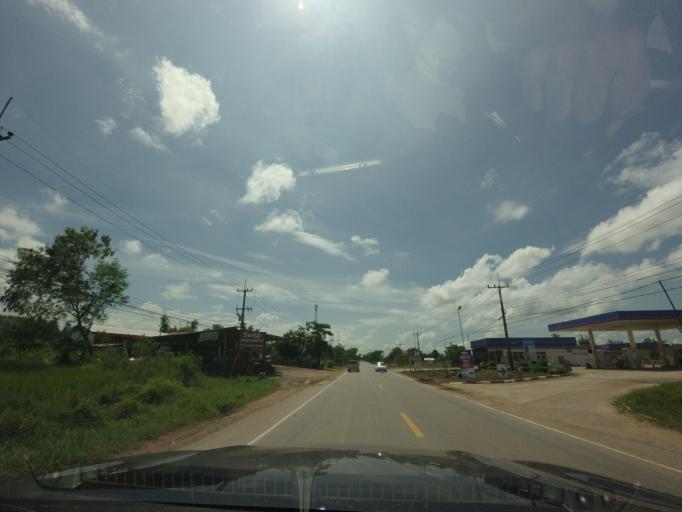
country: TH
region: Nong Khai
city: Pho Tak
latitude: 17.7732
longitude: 102.3958
